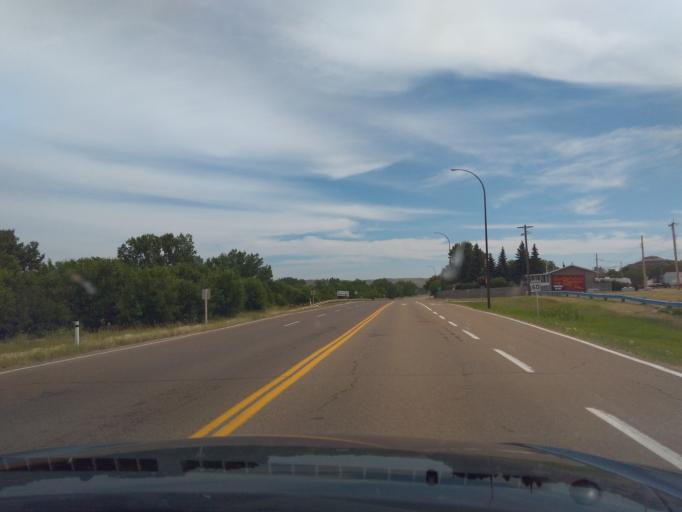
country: CA
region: Alberta
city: Three Hills
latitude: 51.4632
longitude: -112.7489
